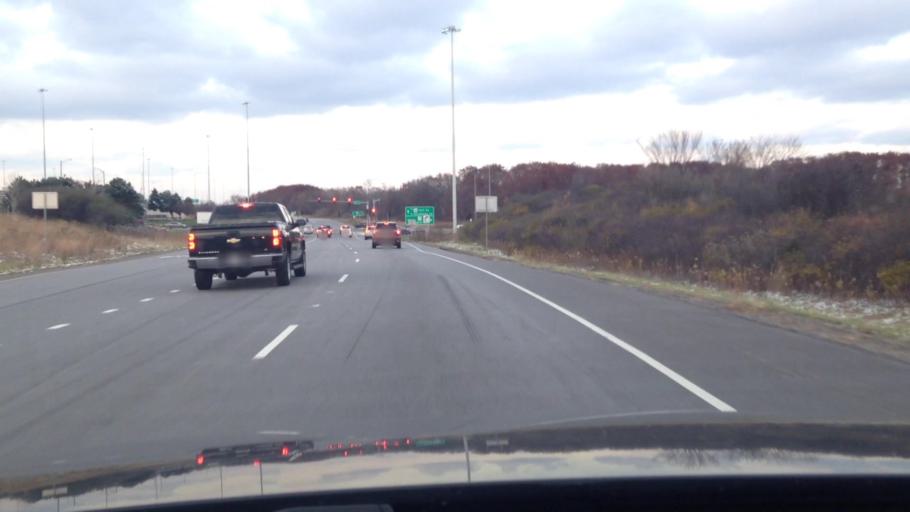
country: US
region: Illinois
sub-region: Cook County
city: Hoffman Estates
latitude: 42.0346
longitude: -88.0298
